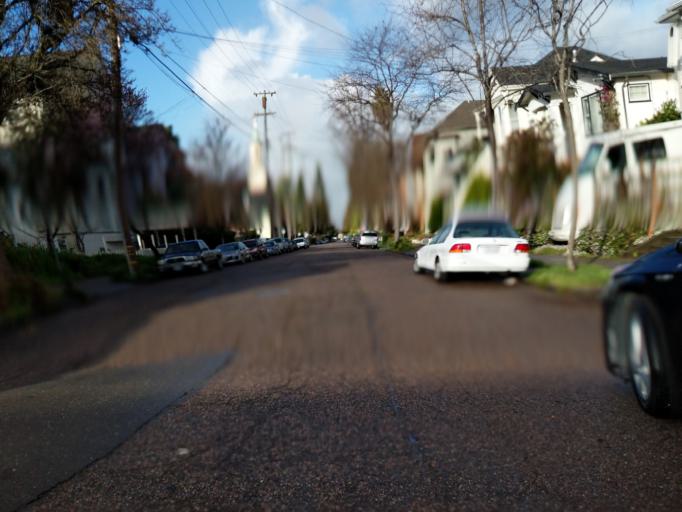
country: US
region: California
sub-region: Alameda County
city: Berkeley
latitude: 37.8577
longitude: -122.2741
